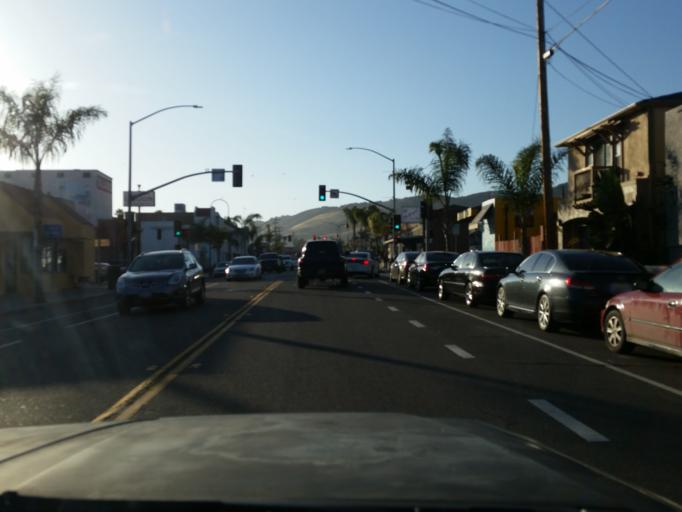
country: US
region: California
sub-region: San Luis Obispo County
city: Pismo Beach
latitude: 35.1397
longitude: -120.6402
